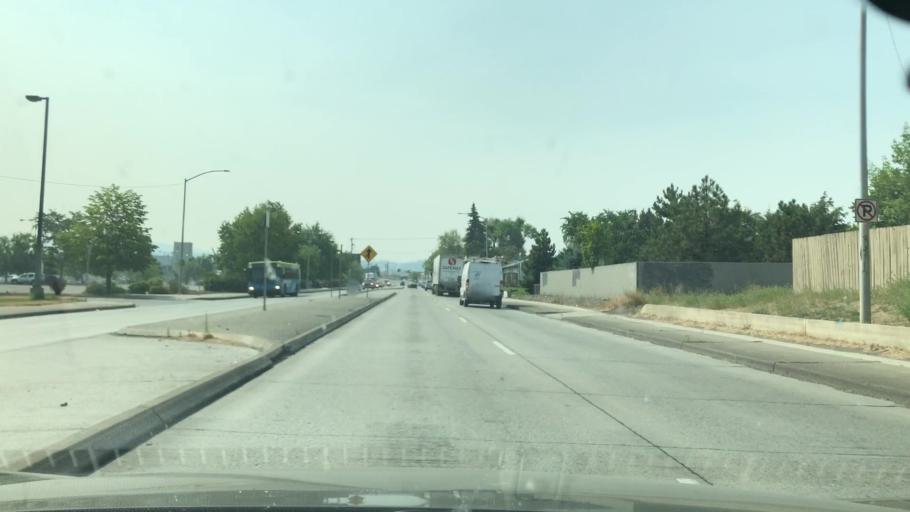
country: US
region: Washington
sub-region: Spokane County
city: Spokane
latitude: 47.6753
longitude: -117.3638
